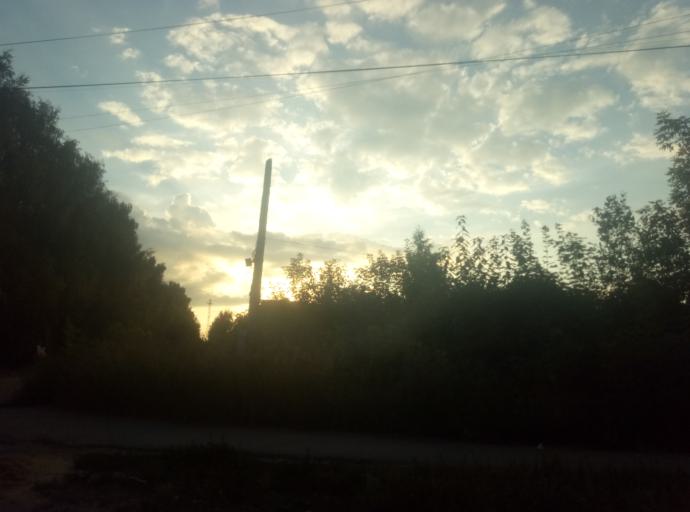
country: RU
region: Tula
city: Kireyevsk
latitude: 53.9227
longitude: 37.9184
